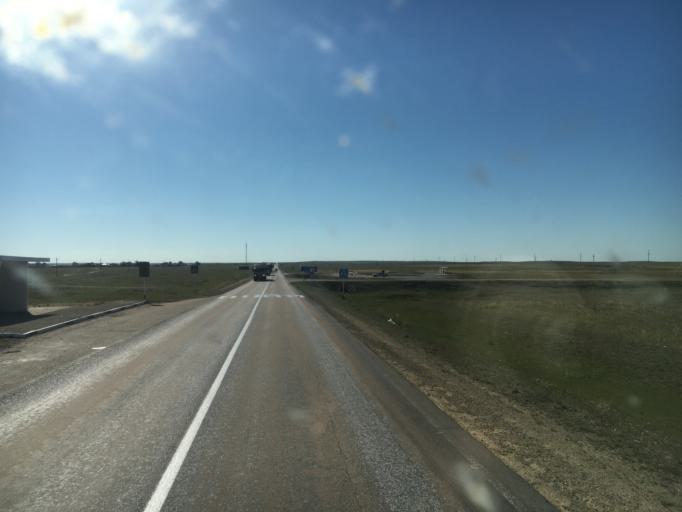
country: RU
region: Orenburg
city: Dombarovskiy
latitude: 50.0703
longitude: 59.6268
